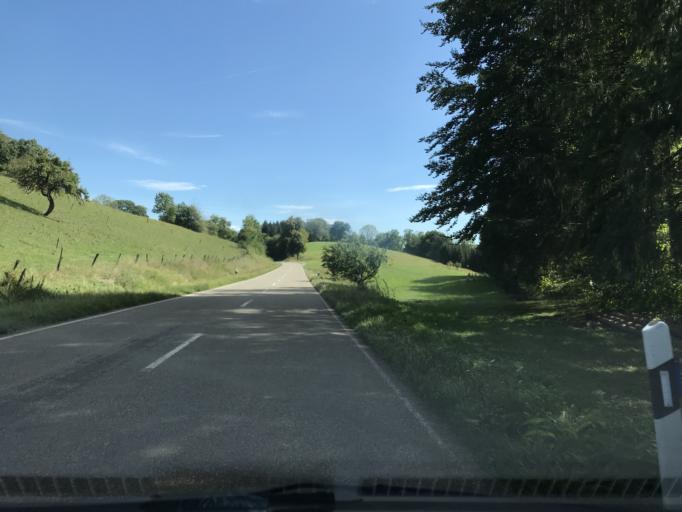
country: DE
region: Baden-Wuerttemberg
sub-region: Freiburg Region
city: Schworstadt
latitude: 47.6227
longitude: 7.8534
